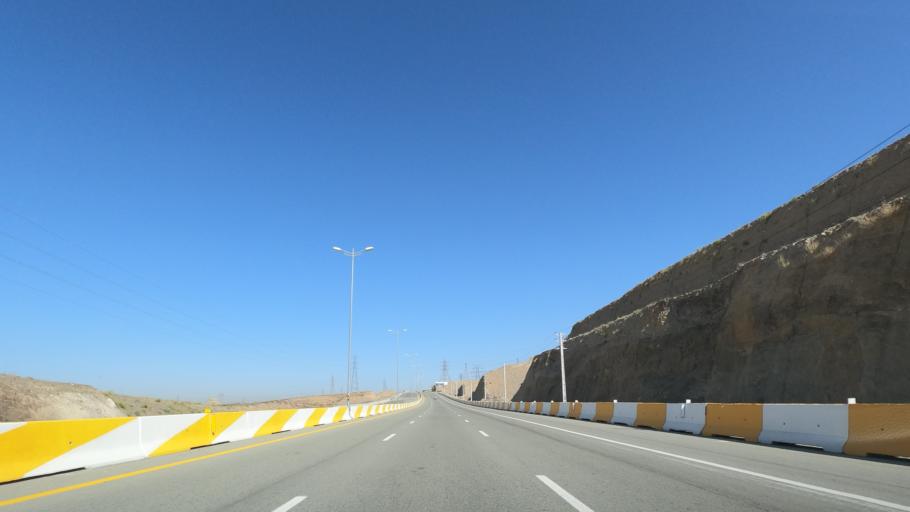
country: IR
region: Tehran
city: Shahr-e Qods
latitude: 35.7712
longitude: 51.0593
